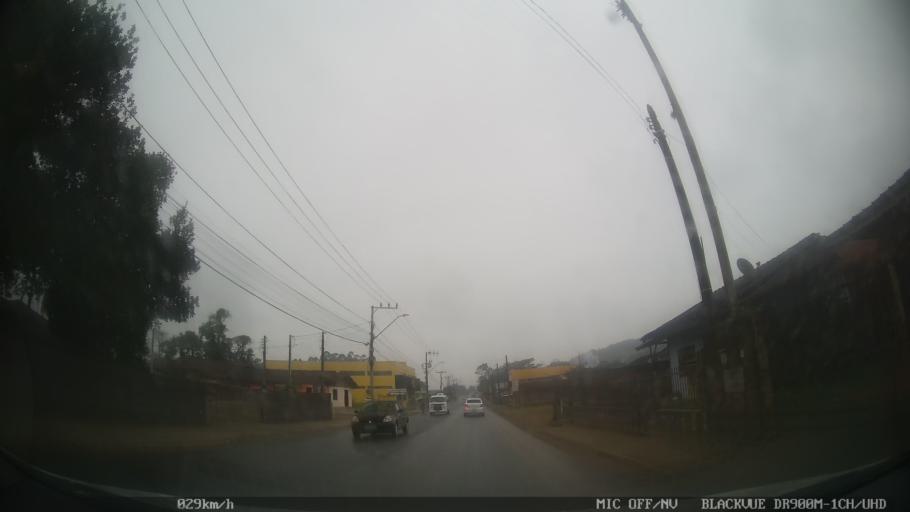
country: BR
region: Santa Catarina
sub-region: Joinville
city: Joinville
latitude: -26.2222
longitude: -48.8216
